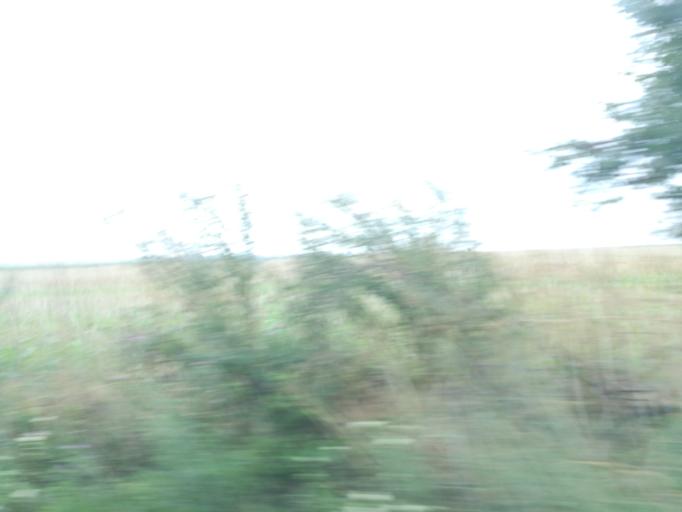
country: RO
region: Constanta
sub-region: Comuna Corbu
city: Corbu
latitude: 44.4240
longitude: 28.6734
